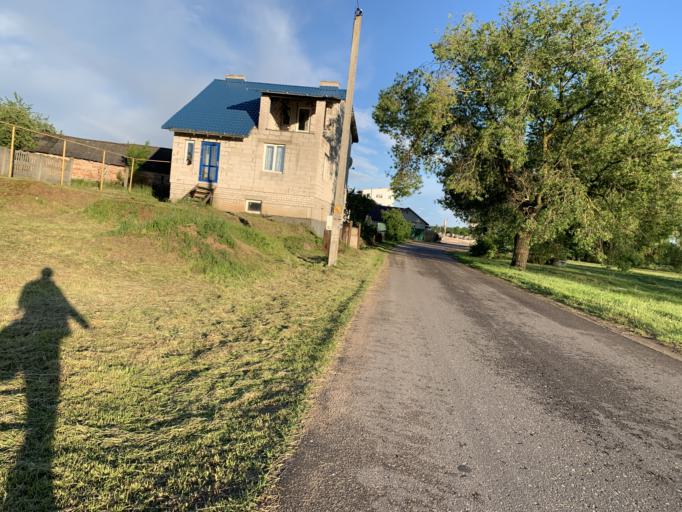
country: BY
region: Minsk
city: Nyasvizh
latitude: 53.2117
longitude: 26.6925
